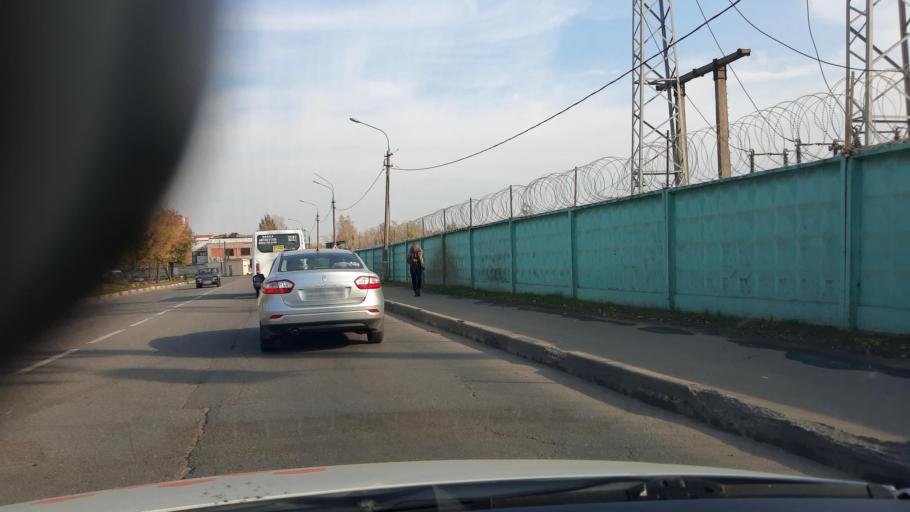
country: RU
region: Moskovskaya
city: Elektrostal'
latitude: 55.7995
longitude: 38.4476
